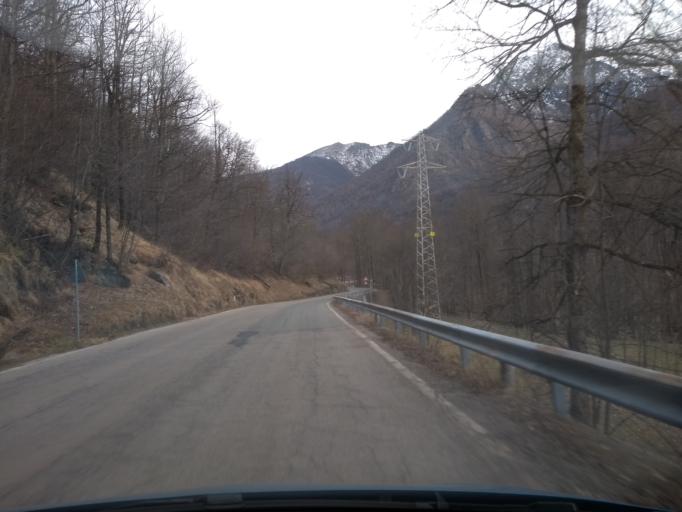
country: IT
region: Piedmont
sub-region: Provincia di Torino
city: Lemie
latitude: 45.2269
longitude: 7.3032
